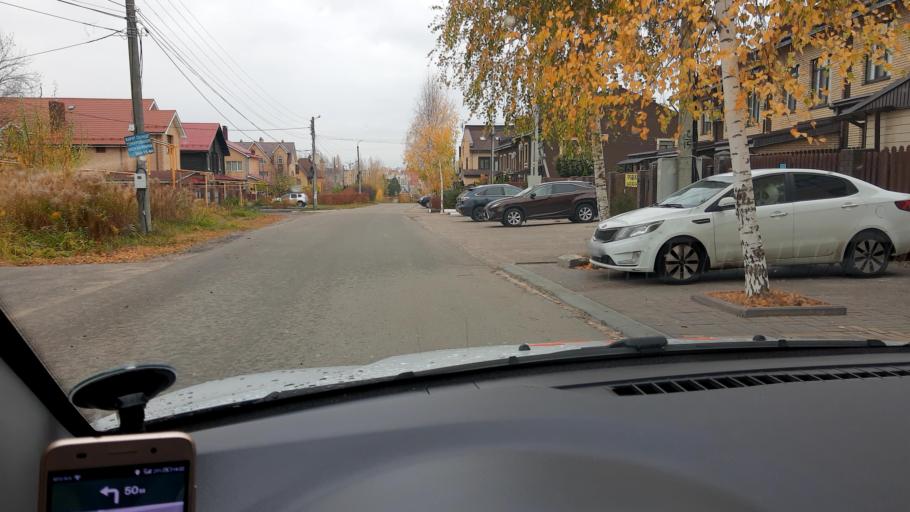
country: RU
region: Nizjnij Novgorod
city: Afonino
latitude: 56.2826
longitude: 44.0642
